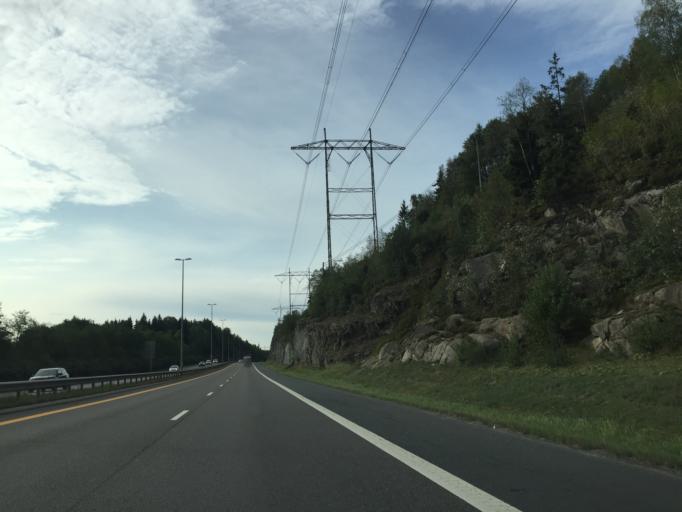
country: NO
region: Akershus
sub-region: Oppegard
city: Kolbotn
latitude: 59.8332
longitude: 10.8402
